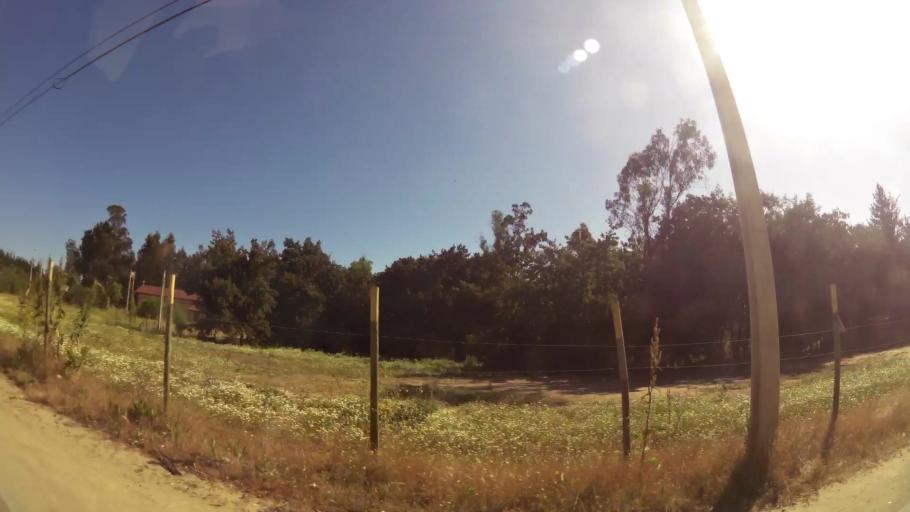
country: CL
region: Valparaiso
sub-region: Provincia de Valparaiso
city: Vina del Mar
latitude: -33.1480
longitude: -71.5607
